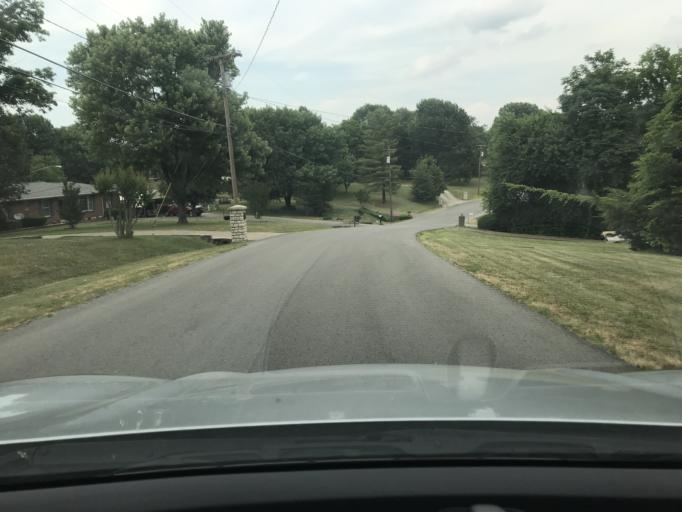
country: US
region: Tennessee
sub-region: Davidson County
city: Goodlettsville
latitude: 36.3113
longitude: -86.7210
